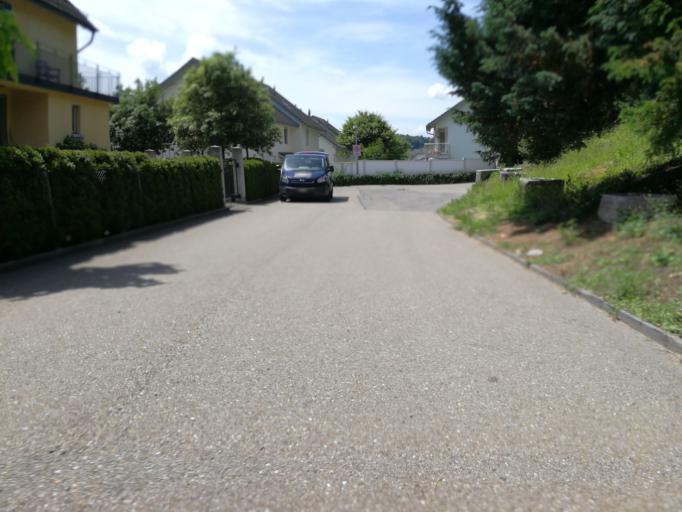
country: CH
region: Saint Gallen
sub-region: Wahlkreis See-Gaster
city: Rapperswil
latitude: 47.2402
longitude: 8.8118
